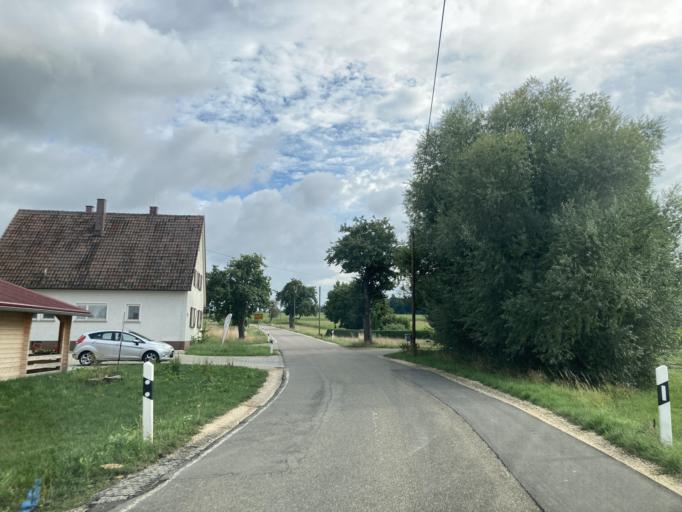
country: DE
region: Bavaria
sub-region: Swabia
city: Bachhagel
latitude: 48.6115
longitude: 10.3073
